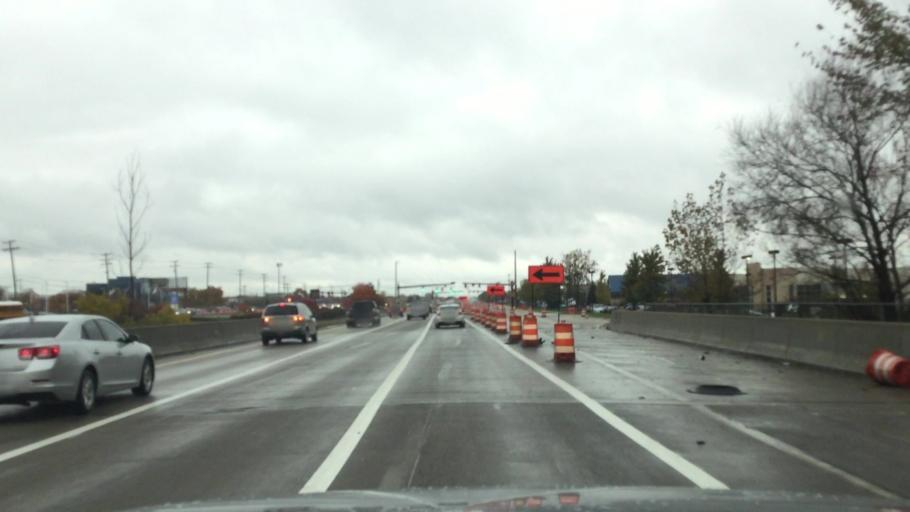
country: US
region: Michigan
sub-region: Macomb County
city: Clinton
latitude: 42.6288
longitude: -82.9309
